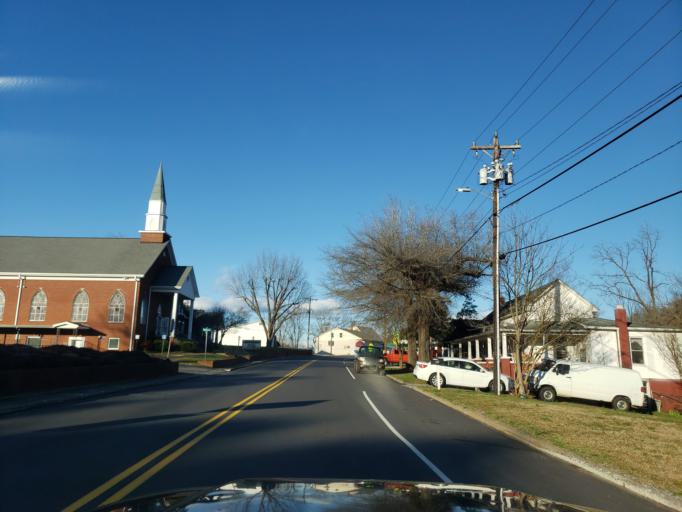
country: US
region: North Carolina
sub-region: Cleveland County
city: Shelby
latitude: 35.4166
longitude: -81.5605
